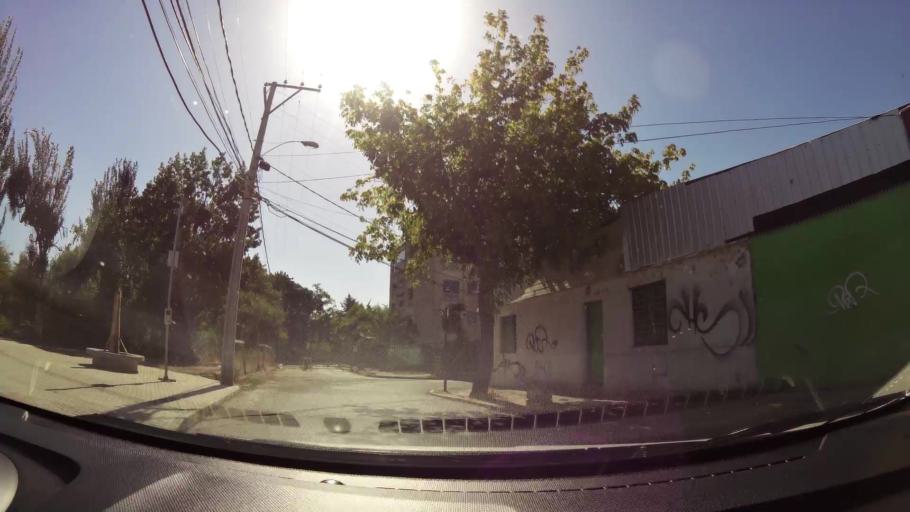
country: CL
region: Maule
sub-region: Provincia de Talca
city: Talca
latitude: -35.4326
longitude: -71.6670
